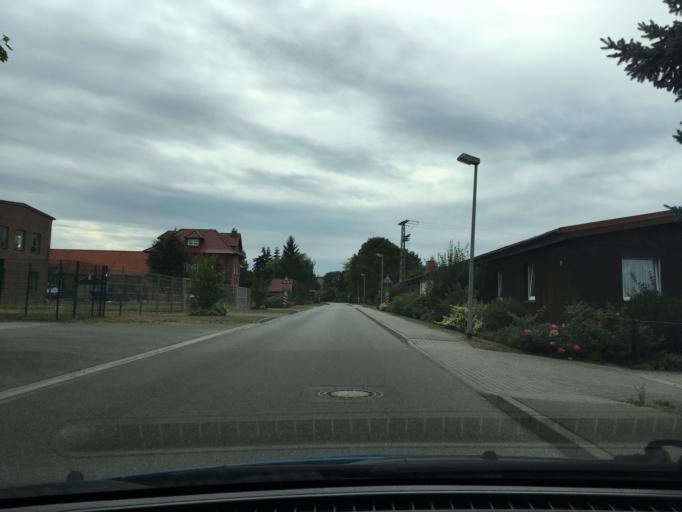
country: DE
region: Mecklenburg-Vorpommern
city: Wittenburg
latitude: 53.5144
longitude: 11.0834
